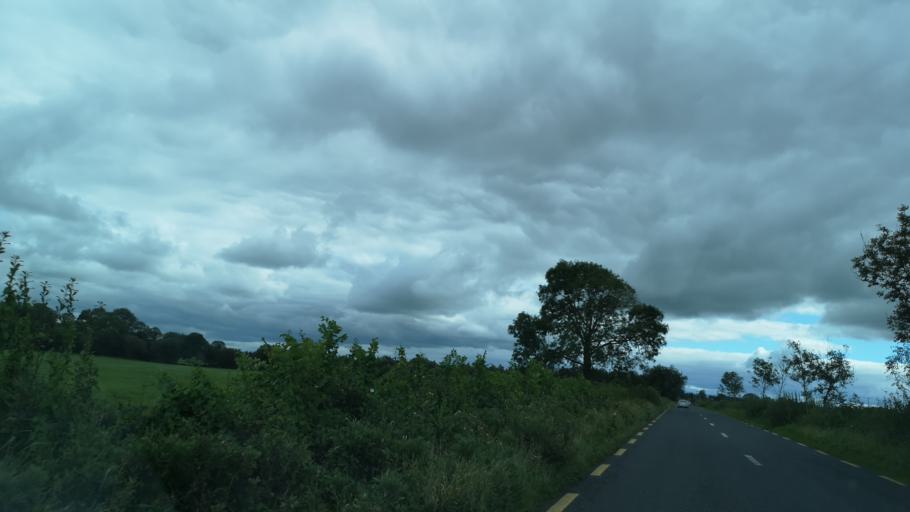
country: IE
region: Leinster
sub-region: Uibh Fhaili
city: Banagher
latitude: 53.2547
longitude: -7.9568
